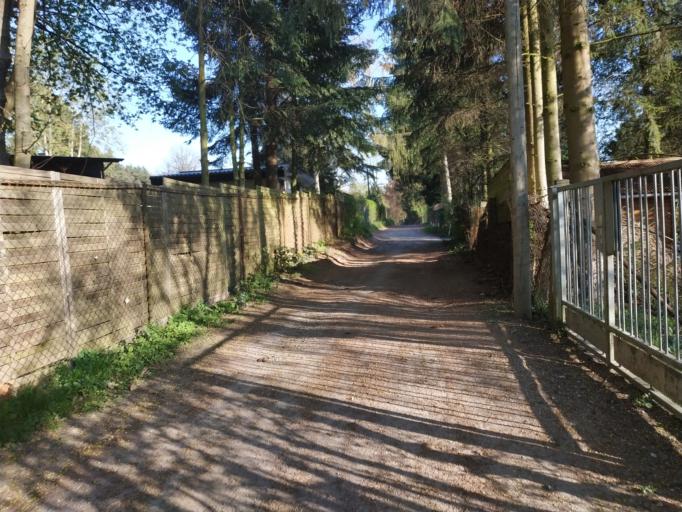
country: DE
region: Brandenburg
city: Strausberg
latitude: 52.5624
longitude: 13.8401
